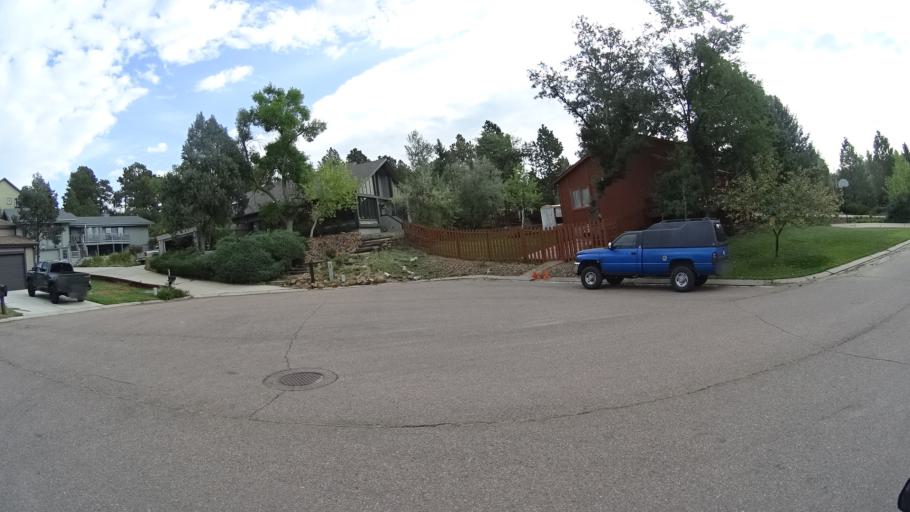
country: US
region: Colorado
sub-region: El Paso County
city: Cimarron Hills
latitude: 38.8674
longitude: -104.7500
